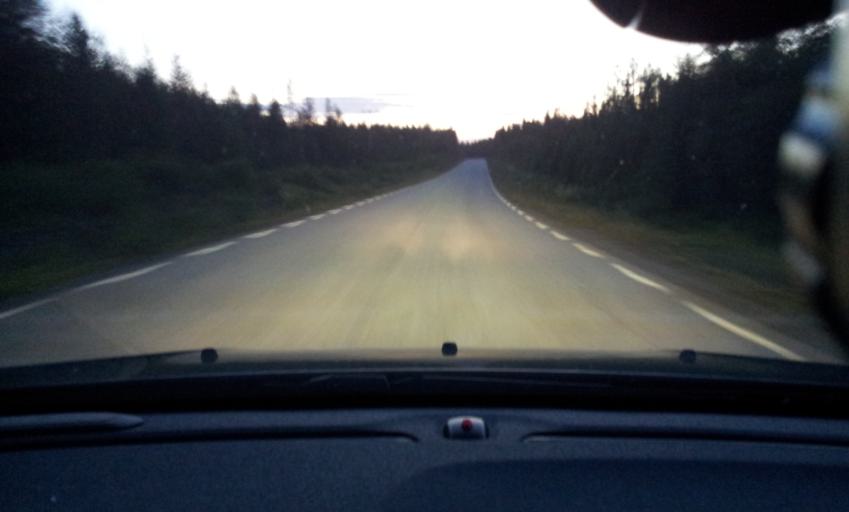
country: SE
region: Jaemtland
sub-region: Bergs Kommun
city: Hoverberg
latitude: 62.7119
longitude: 14.6102
